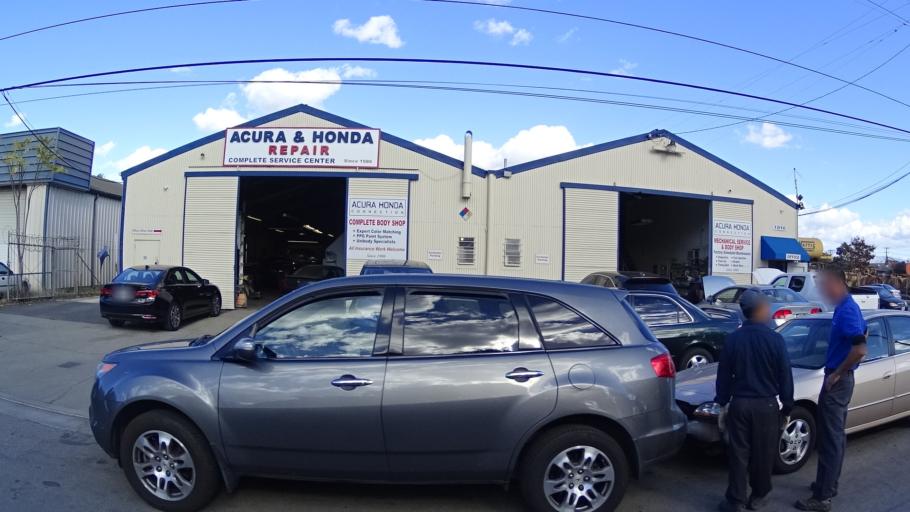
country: US
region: California
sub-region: Santa Clara County
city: Buena Vista
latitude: 37.3466
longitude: -121.9199
